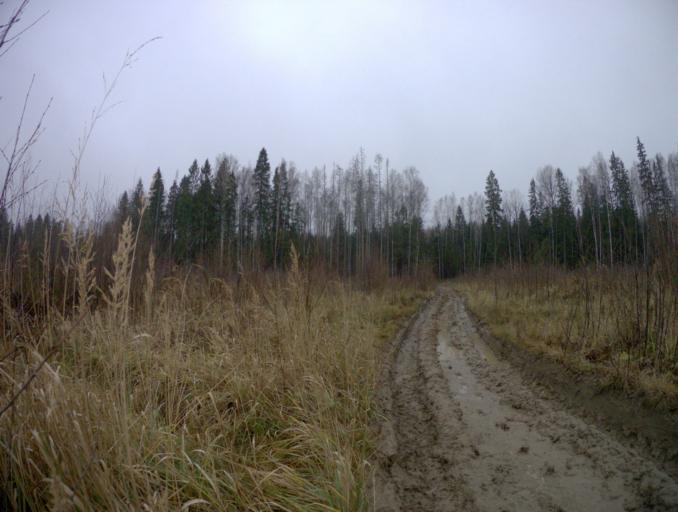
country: RU
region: Vladimir
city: Golovino
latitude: 56.0005
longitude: 40.4716
